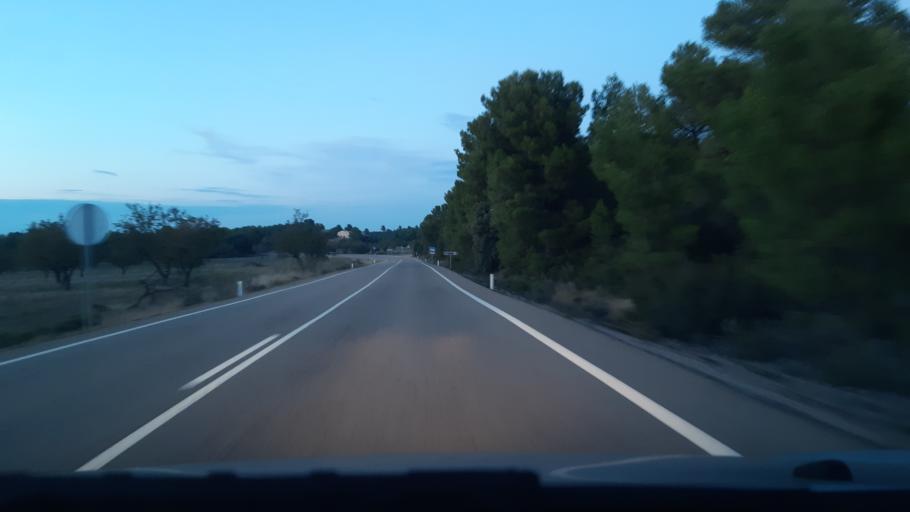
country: ES
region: Aragon
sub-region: Provincia de Teruel
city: Lledo
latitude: 40.9501
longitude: 0.2233
